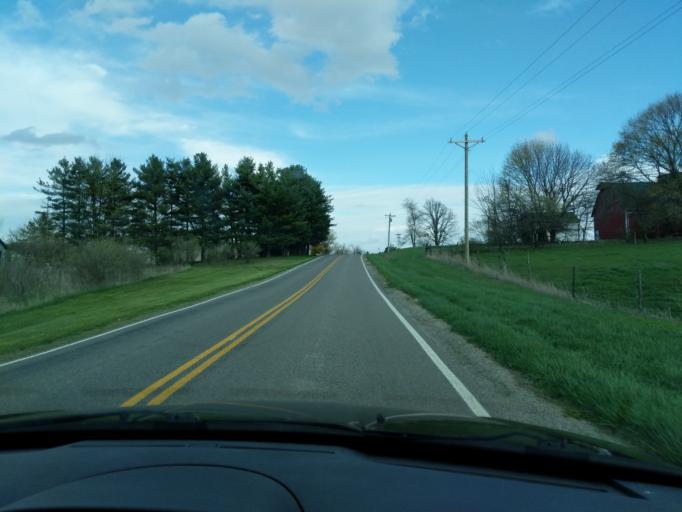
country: US
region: Ohio
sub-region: Champaign County
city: Urbana
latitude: 40.1556
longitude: -83.6587
